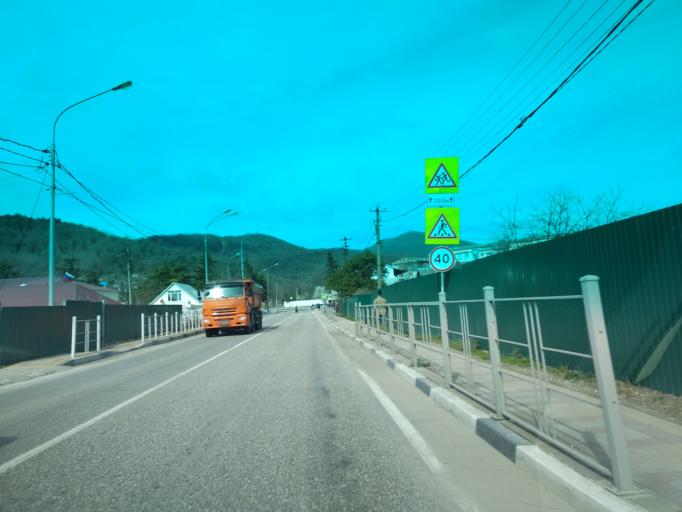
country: RU
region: Krasnodarskiy
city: Shepsi
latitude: 44.0403
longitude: 39.1507
